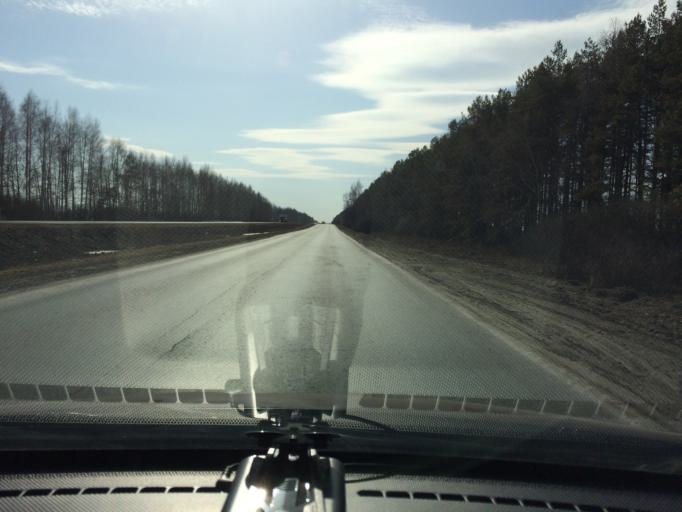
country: RU
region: Mariy-El
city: Yoshkar-Ola
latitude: 56.7311
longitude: 48.1474
